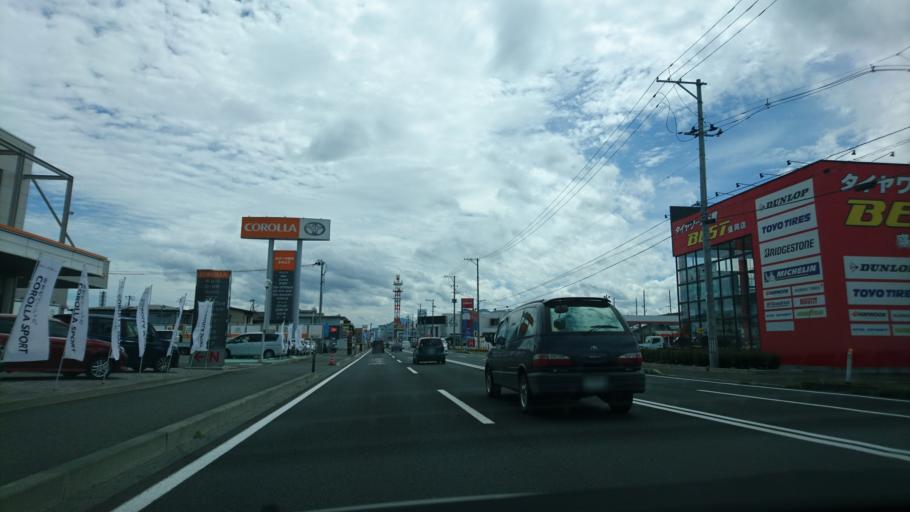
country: JP
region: Iwate
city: Morioka-shi
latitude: 39.7353
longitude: 141.1249
